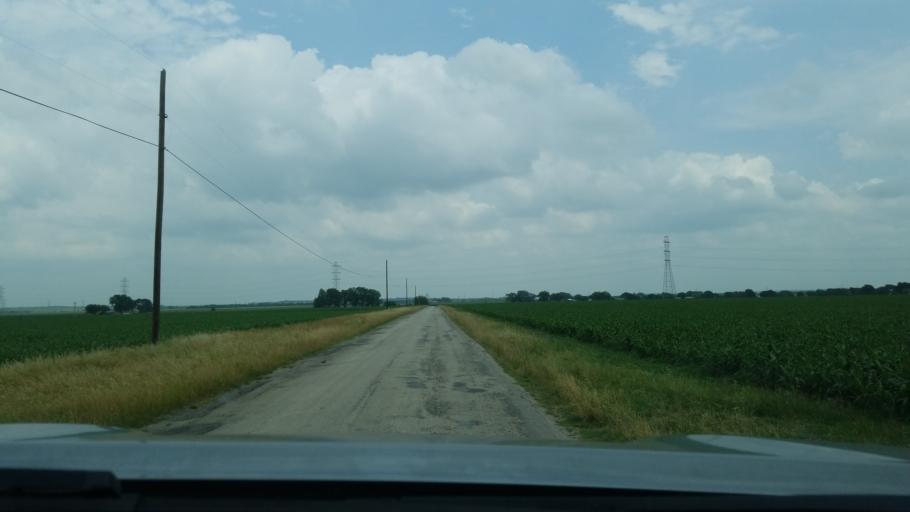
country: US
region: Texas
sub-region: Guadalupe County
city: Lake Dunlap
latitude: 29.6763
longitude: -98.0209
